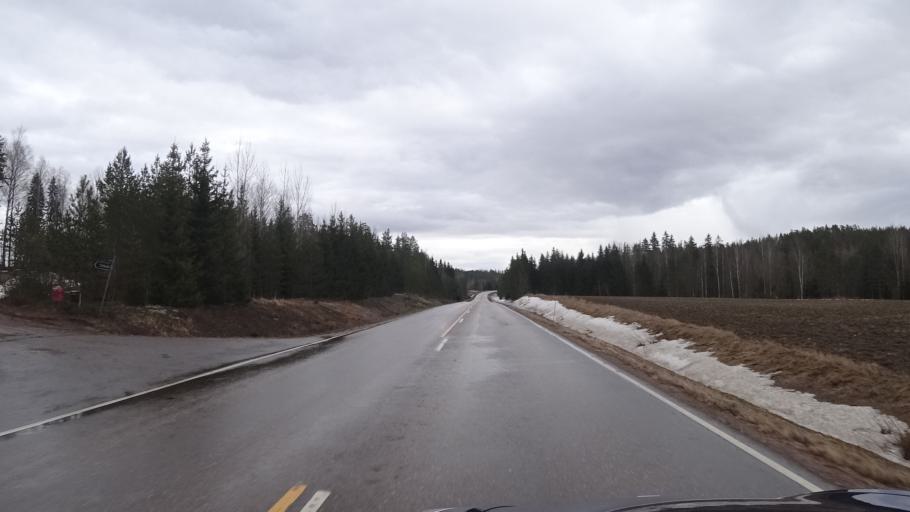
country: FI
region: Uusimaa
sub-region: Loviisa
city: Lapinjaervi
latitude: 60.7324
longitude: 26.2155
